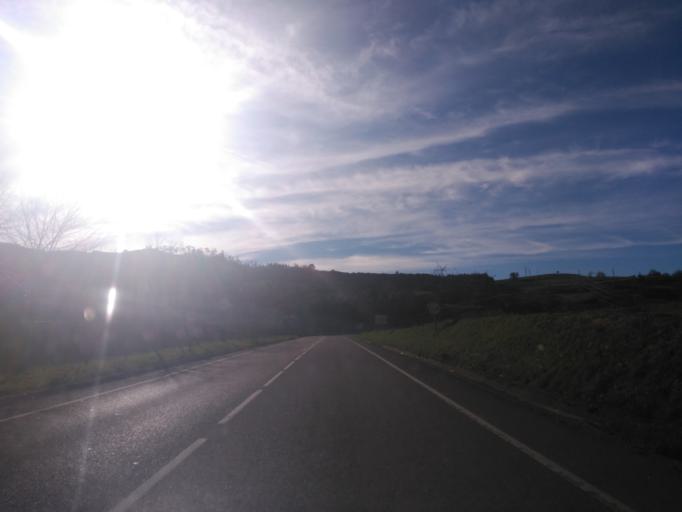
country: ES
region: Cantabria
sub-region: Provincia de Cantabria
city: Comillas
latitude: 43.3528
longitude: -4.2656
